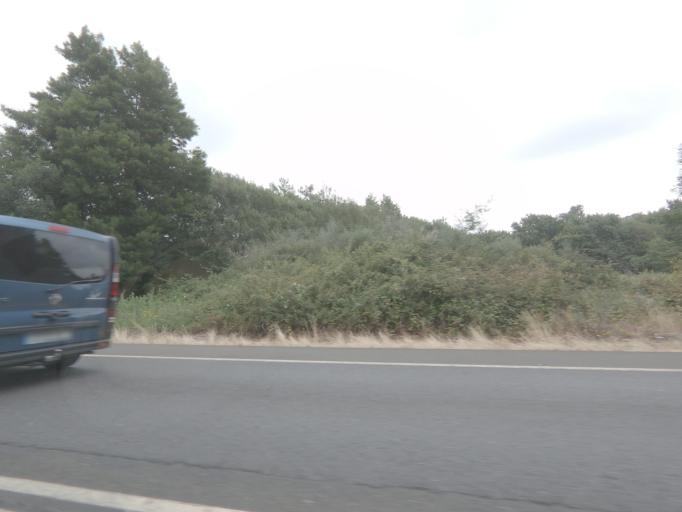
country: ES
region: Galicia
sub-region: Provincia de Pontevedra
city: Tomino
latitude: 41.9669
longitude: -8.7592
